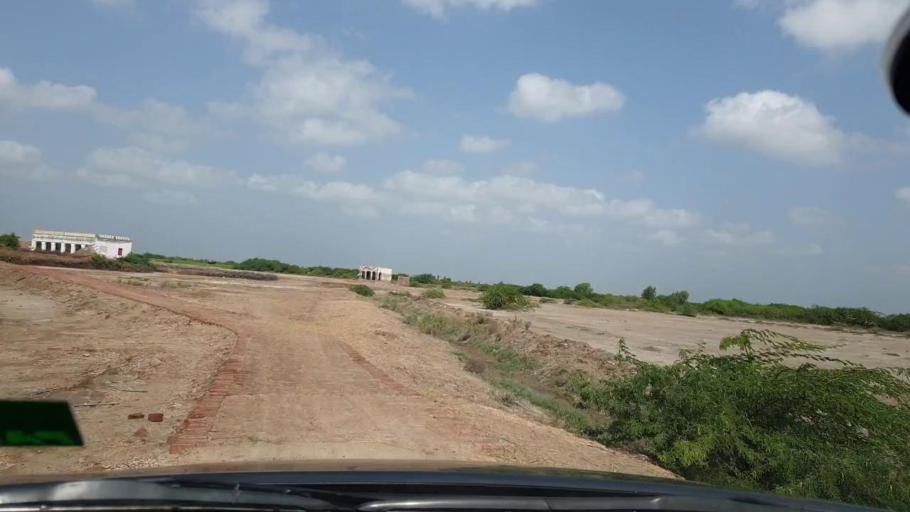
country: PK
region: Sindh
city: Kadhan
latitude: 24.6315
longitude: 69.1442
